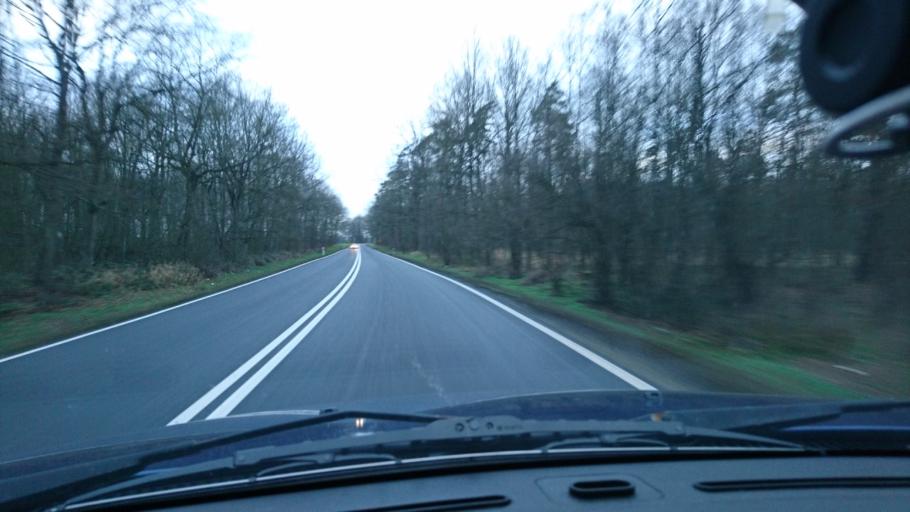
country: PL
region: Opole Voivodeship
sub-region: Powiat kluczborski
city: Byczyna
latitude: 51.1463
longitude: 18.1903
